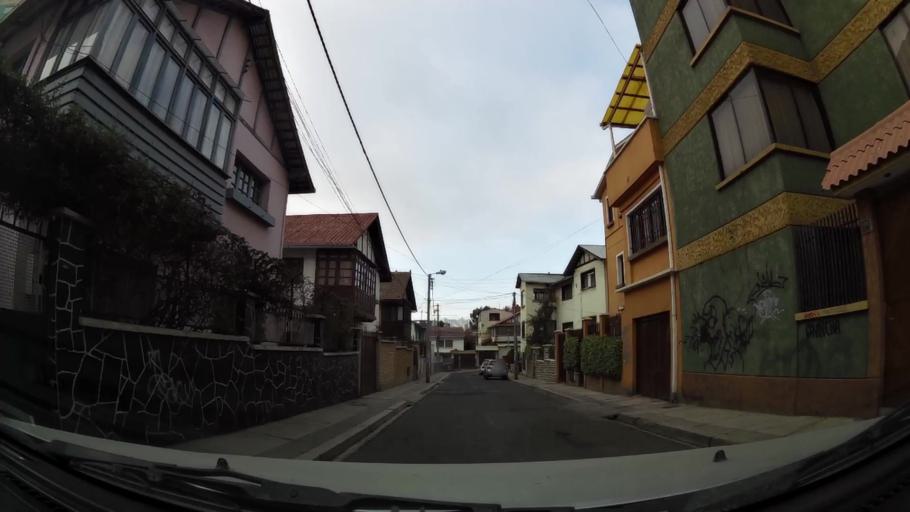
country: BO
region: La Paz
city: La Paz
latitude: -16.5022
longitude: -68.1233
